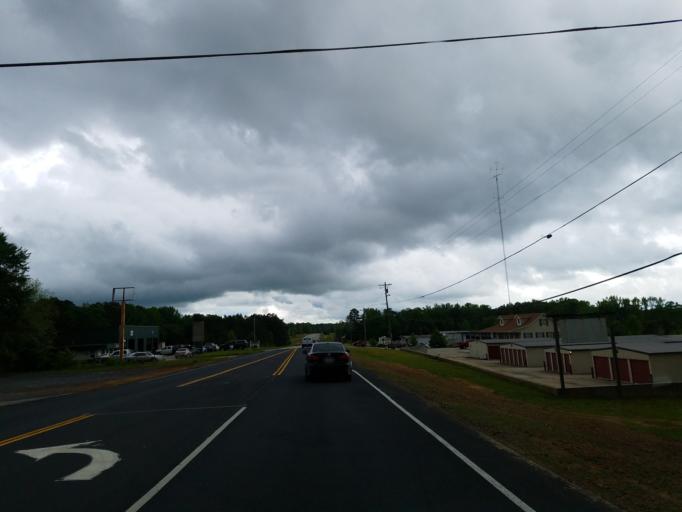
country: US
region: Georgia
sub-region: Lamar County
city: Barnesville
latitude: 33.0343
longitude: -84.1500
